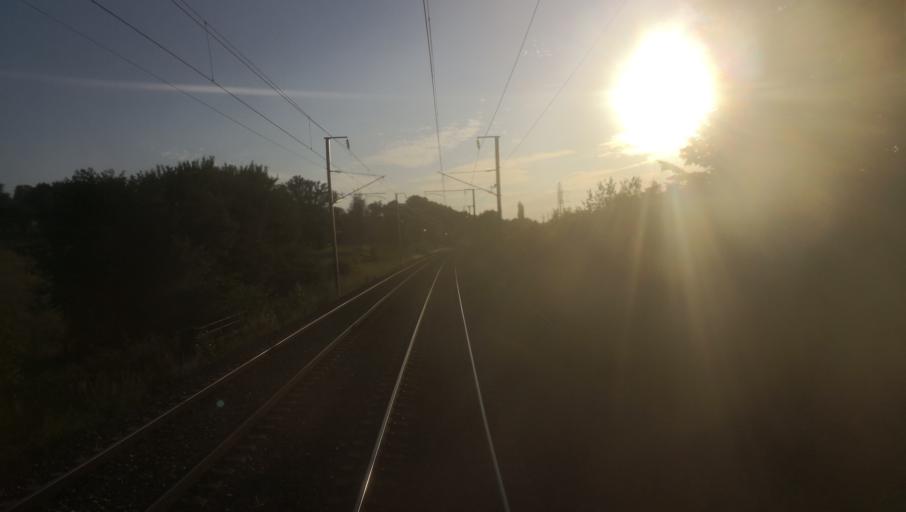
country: FR
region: Lower Normandy
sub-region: Departement du Calvados
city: Beuvillers
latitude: 49.1232
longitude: 0.3052
